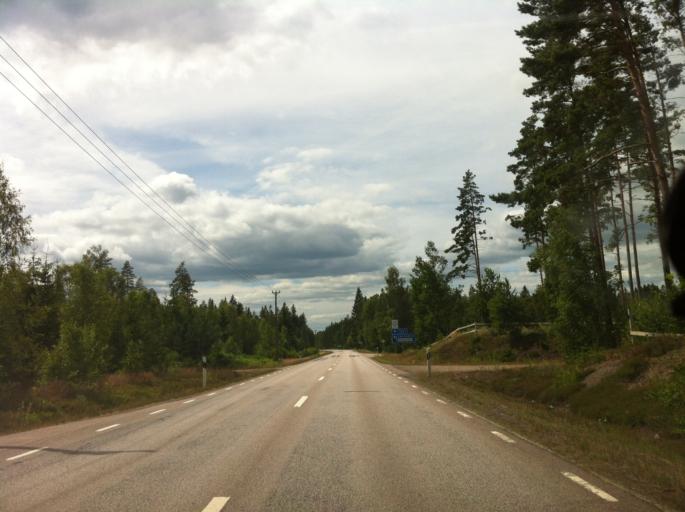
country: SE
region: Kalmar
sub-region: Emmaboda Kommun
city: Emmaboda
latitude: 56.6262
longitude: 15.6115
